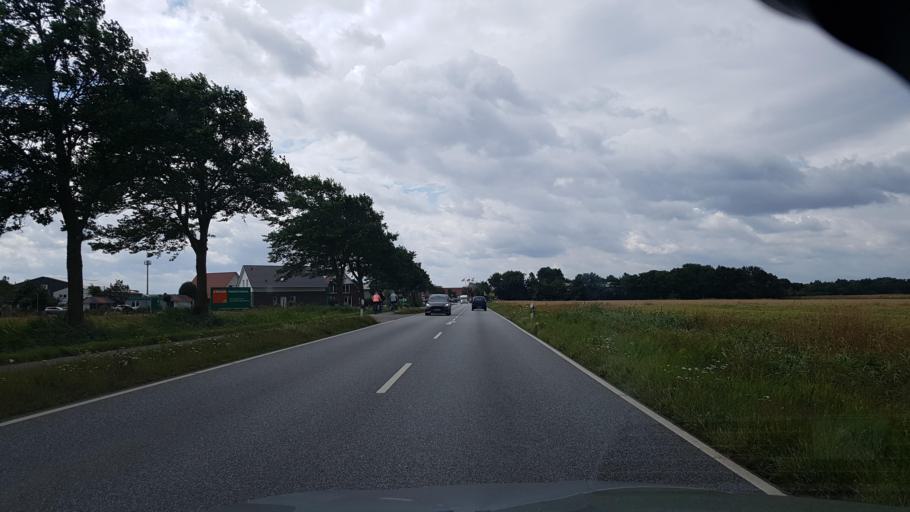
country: DE
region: Schleswig-Holstein
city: Busumer Deichhausen
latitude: 54.1417
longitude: 8.8750
